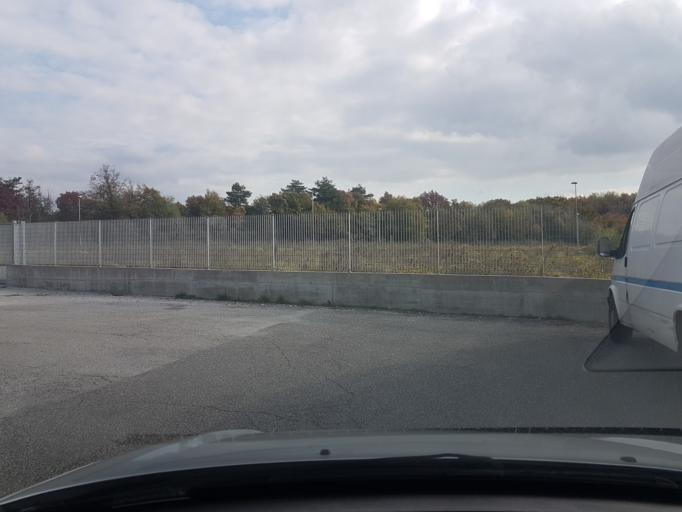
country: IT
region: Friuli Venezia Giulia
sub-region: Provincia di Trieste
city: Sistiana-Visogliano
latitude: 45.7683
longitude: 13.6455
